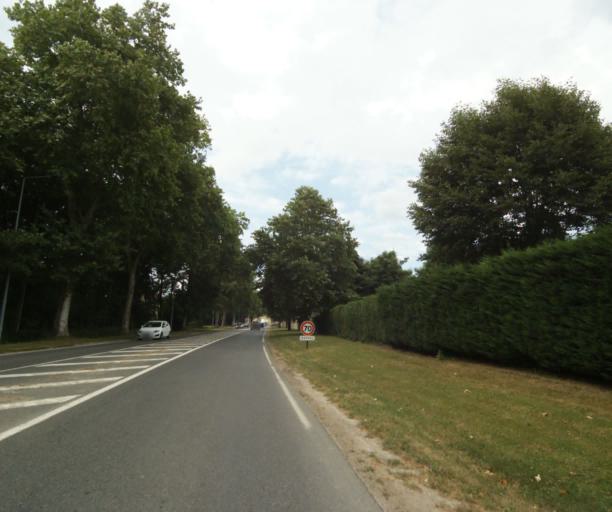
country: FR
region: Ile-de-France
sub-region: Departement de Seine-et-Marne
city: Chailly-en-Biere
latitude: 48.4624
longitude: 2.6080
